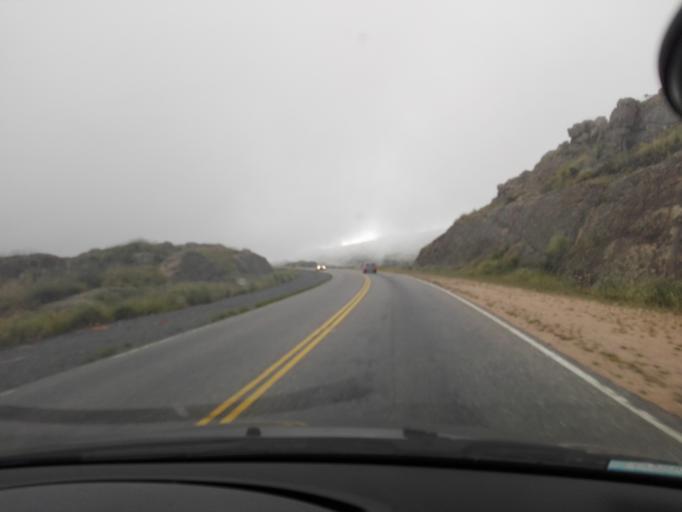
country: AR
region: Cordoba
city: Cuesta Blanca
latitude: -31.6102
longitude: -64.7391
